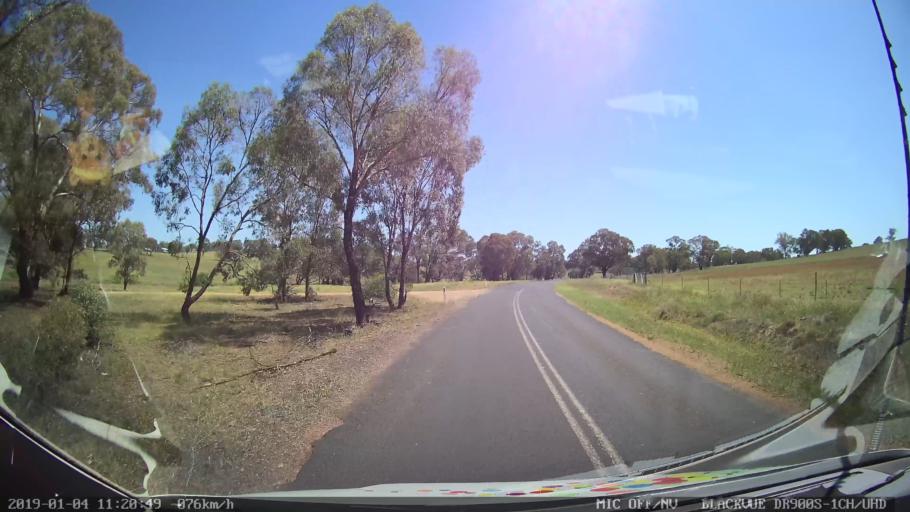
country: AU
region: New South Wales
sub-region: Cabonne
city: Molong
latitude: -33.1600
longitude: 148.7059
